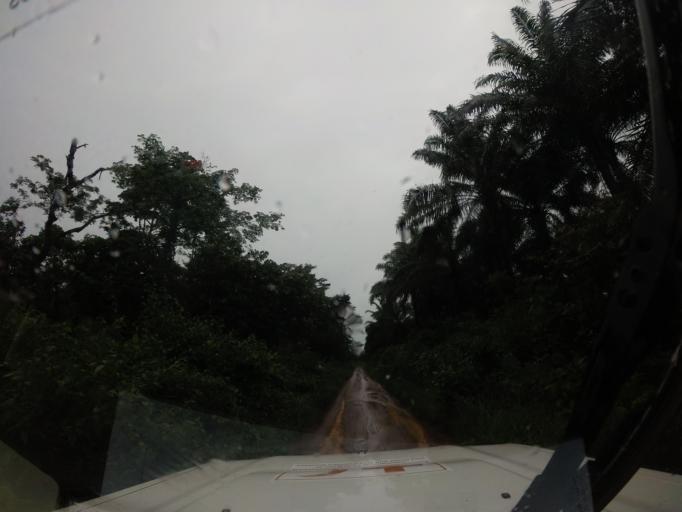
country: SL
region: Eastern Province
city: Kenema
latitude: 7.7445
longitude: -11.2065
